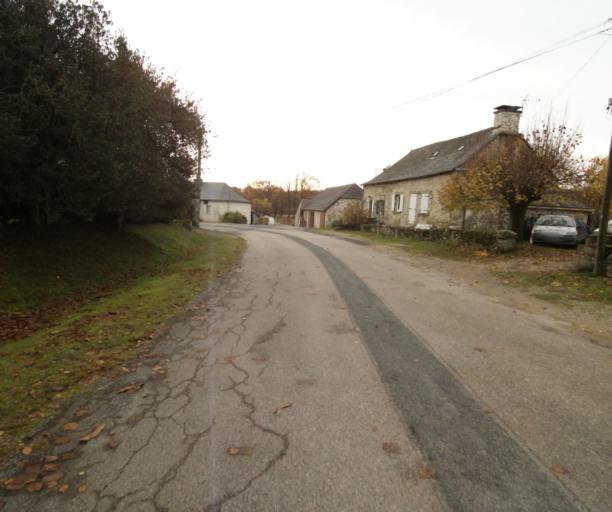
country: FR
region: Limousin
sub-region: Departement de la Correze
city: Sainte-Fortunade
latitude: 45.1738
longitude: 1.7547
